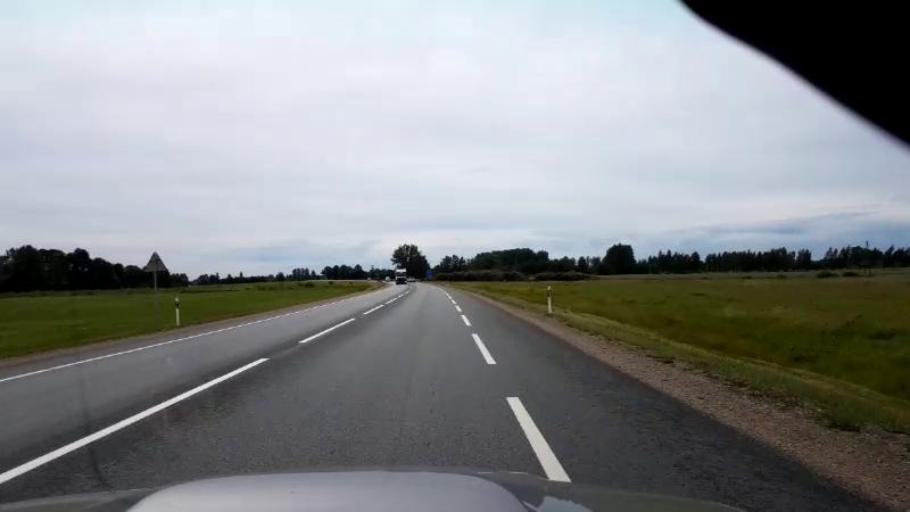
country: LV
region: Lecava
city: Iecava
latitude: 56.5785
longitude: 24.1789
